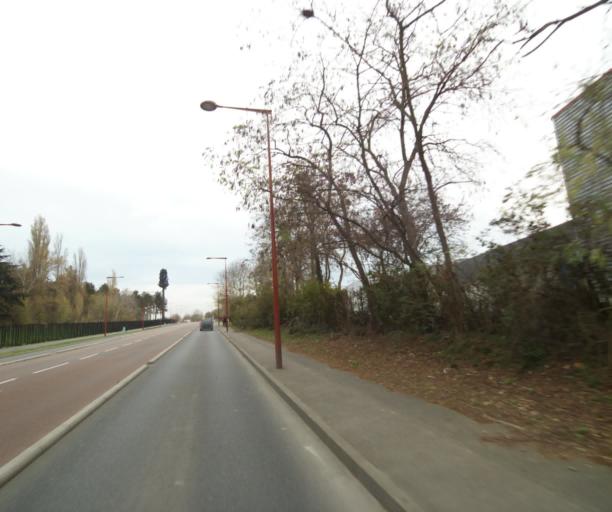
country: FR
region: Ile-de-France
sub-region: Departement du Val-d'Oise
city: Gonesse
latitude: 48.9841
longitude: 2.4655
